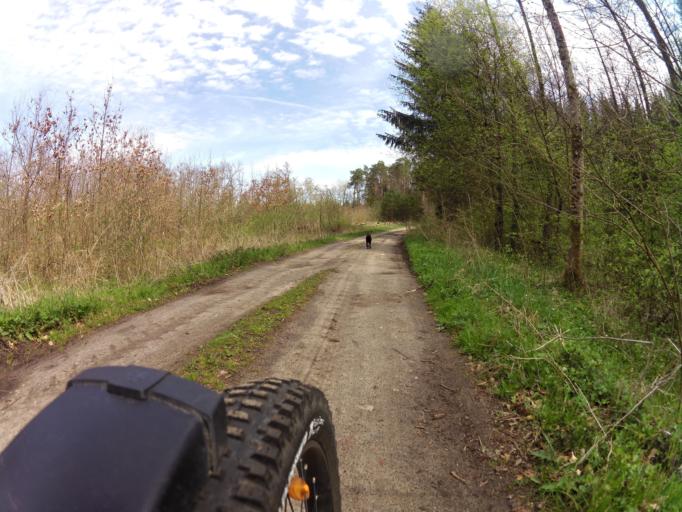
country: PL
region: West Pomeranian Voivodeship
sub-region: Powiat lobeski
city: Resko
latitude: 53.7570
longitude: 15.3624
